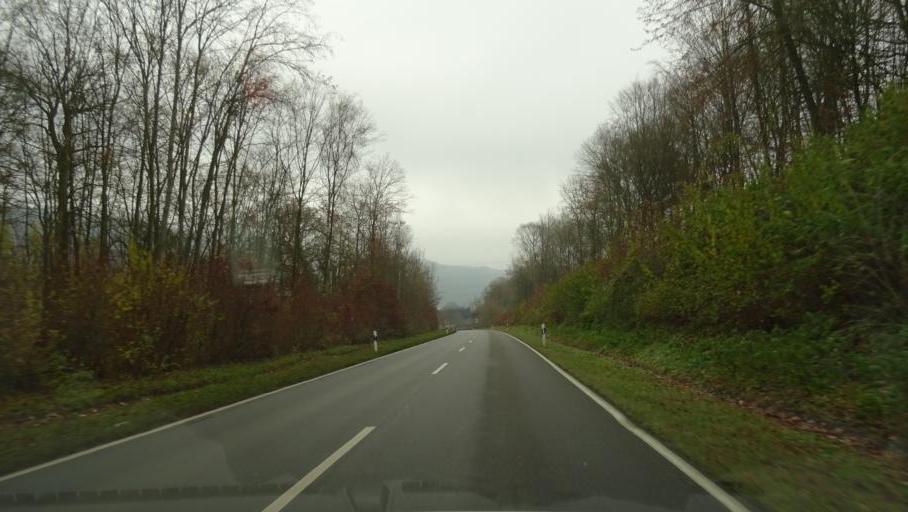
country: DE
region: Baden-Wuerttemberg
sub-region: Karlsruhe Region
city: Neckarzimmern
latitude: 49.3160
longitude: 9.1266
